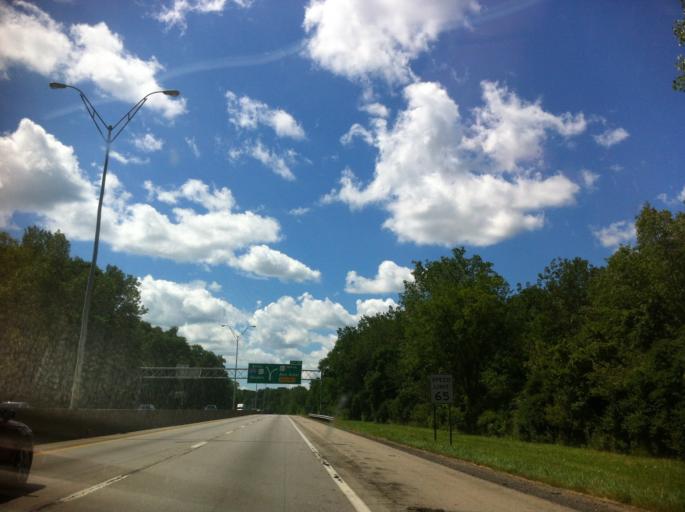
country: US
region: Ohio
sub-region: Lucas County
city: Ottawa Hills
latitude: 41.6898
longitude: -83.6726
